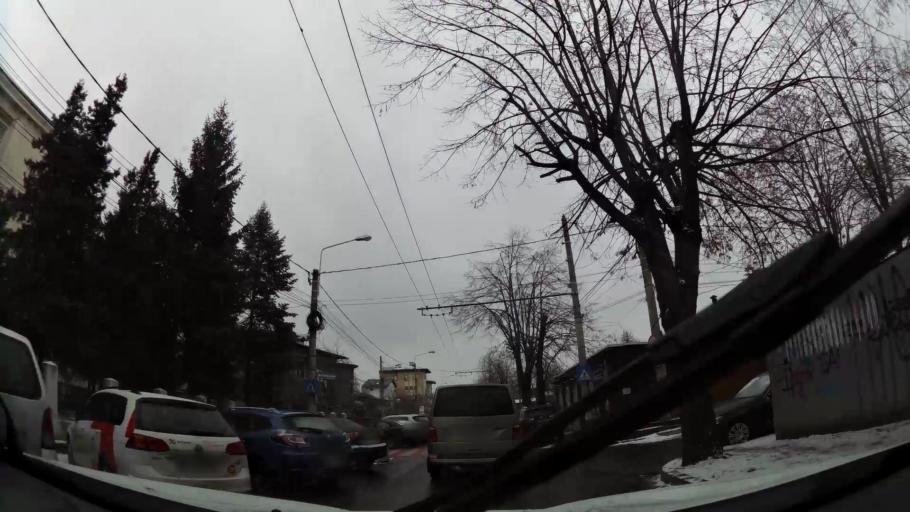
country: RO
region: Prahova
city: Ploiesti
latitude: 44.9405
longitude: 26.0164
